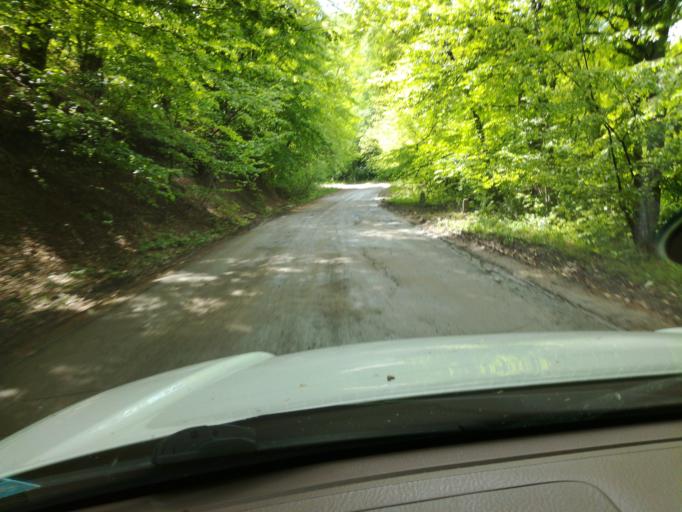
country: AM
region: Lorri
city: Dsegh
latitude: 40.9511
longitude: 44.6966
